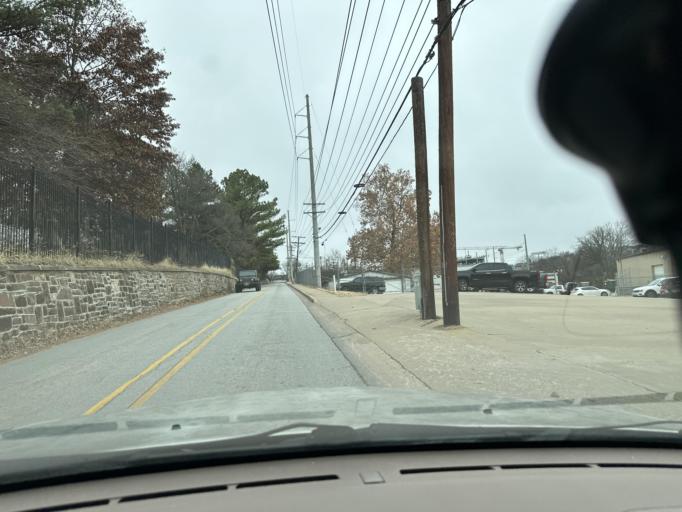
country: US
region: Arkansas
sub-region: Washington County
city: Fayetteville
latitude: 36.0633
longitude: -94.1682
